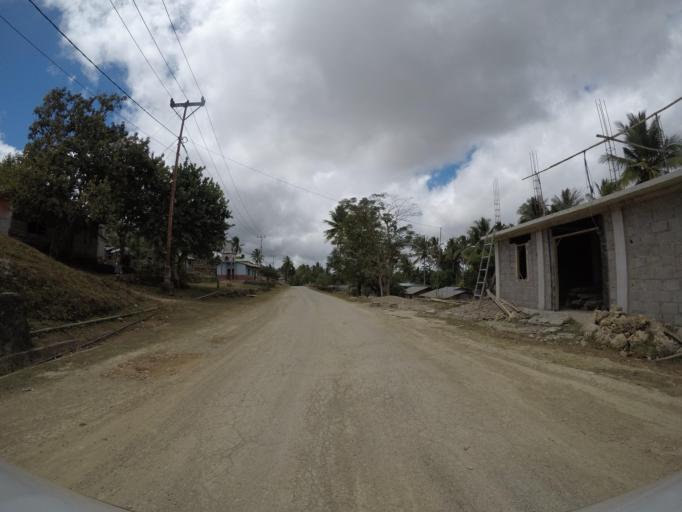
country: TL
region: Lautem
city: Lospalos
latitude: -8.4412
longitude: 126.9679
